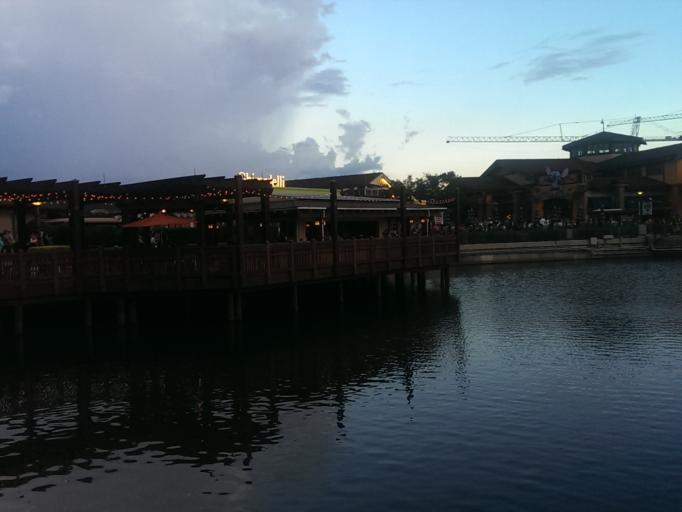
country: US
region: Florida
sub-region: Osceola County
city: Celebration
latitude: 28.3725
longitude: -81.5150
